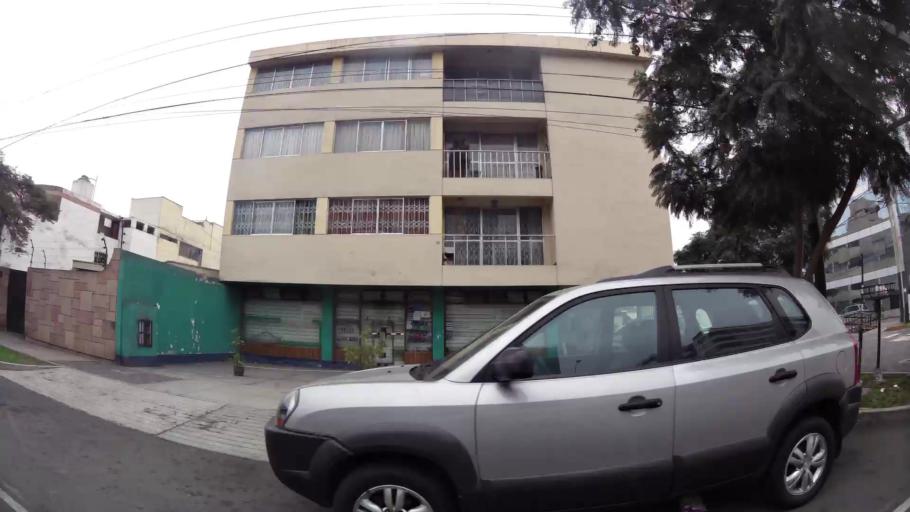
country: PE
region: Lima
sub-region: Lima
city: San Luis
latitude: -12.1055
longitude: -77.0110
